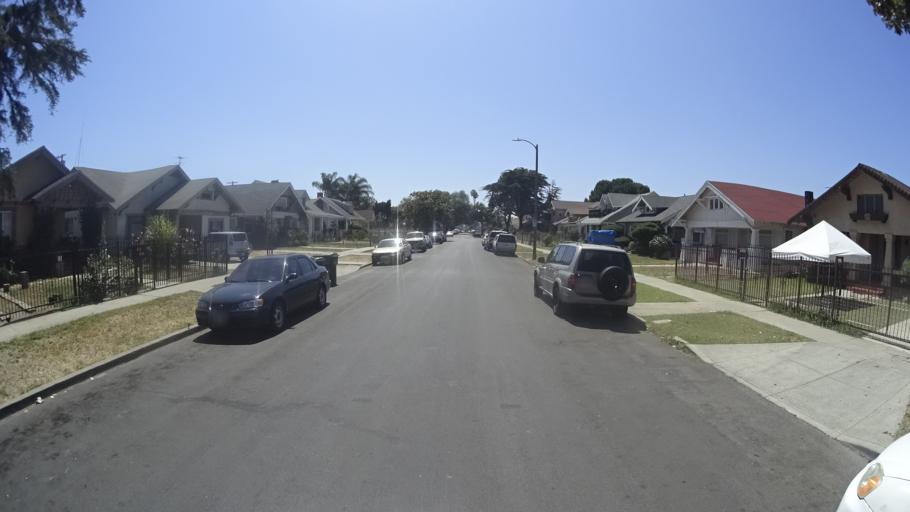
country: US
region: California
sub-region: Los Angeles County
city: View Park-Windsor Hills
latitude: 33.9986
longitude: -118.2926
